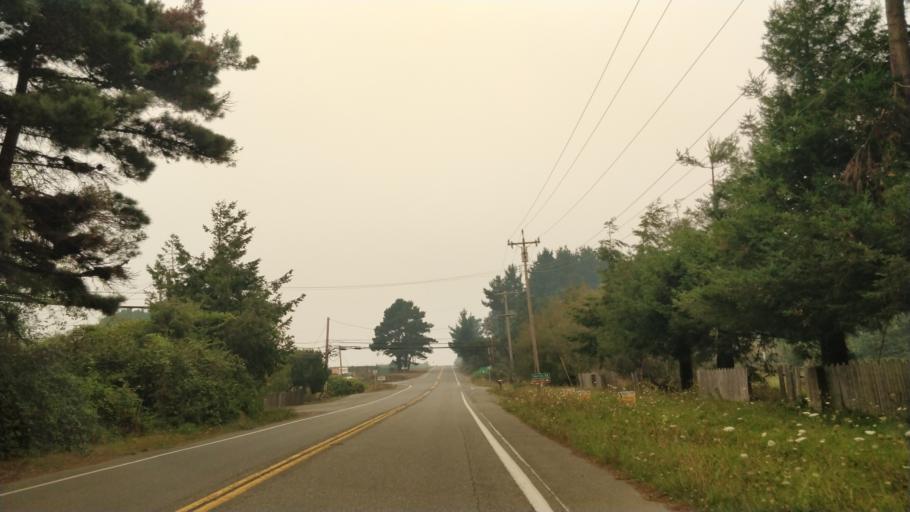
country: US
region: California
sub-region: Humboldt County
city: McKinleyville
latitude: 40.9625
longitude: -124.1009
